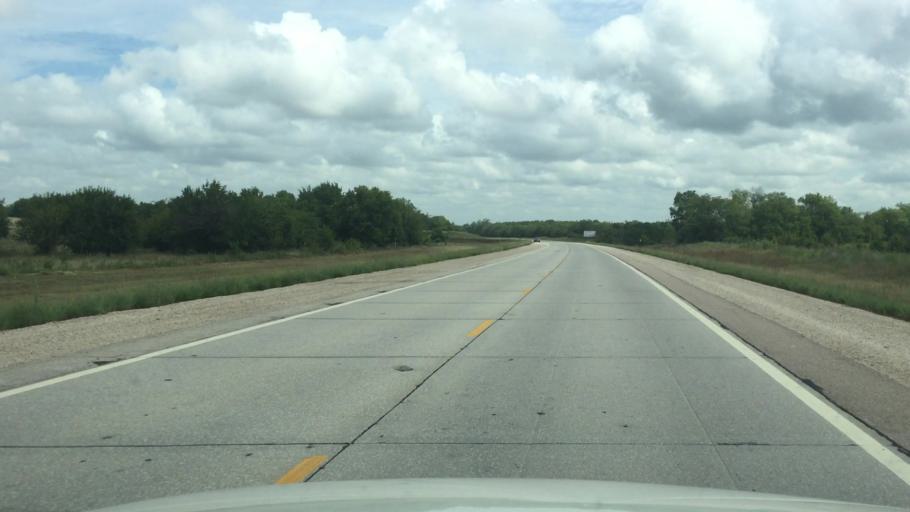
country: US
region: Kansas
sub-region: Allen County
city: Iola
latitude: 37.8950
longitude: -95.3850
